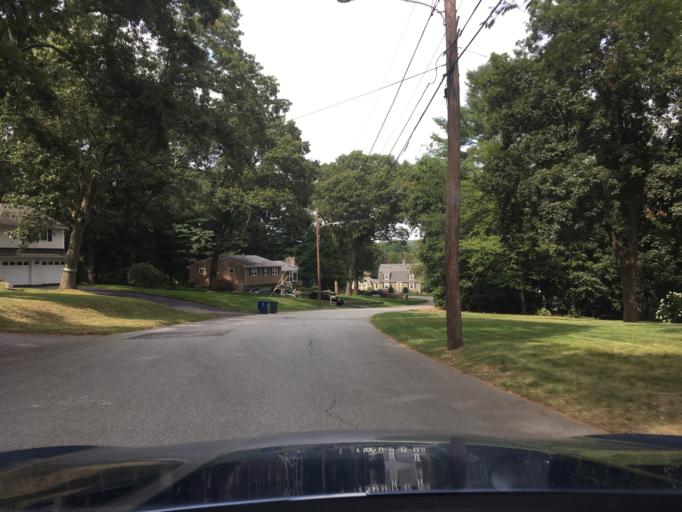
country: US
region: Rhode Island
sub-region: Kent County
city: East Greenwich
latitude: 41.6574
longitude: -71.4687
